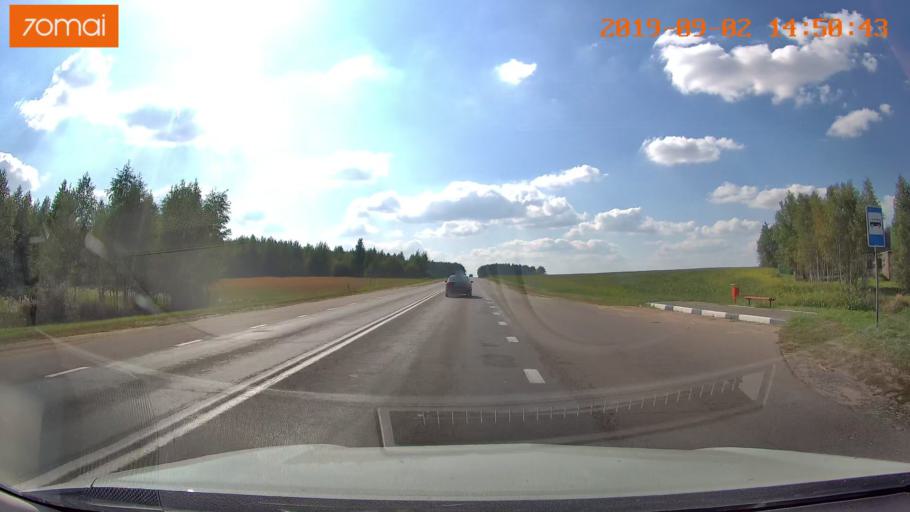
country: BY
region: Mogilev
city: Palykavichy Pyershyya
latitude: 53.9799
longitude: 30.3024
